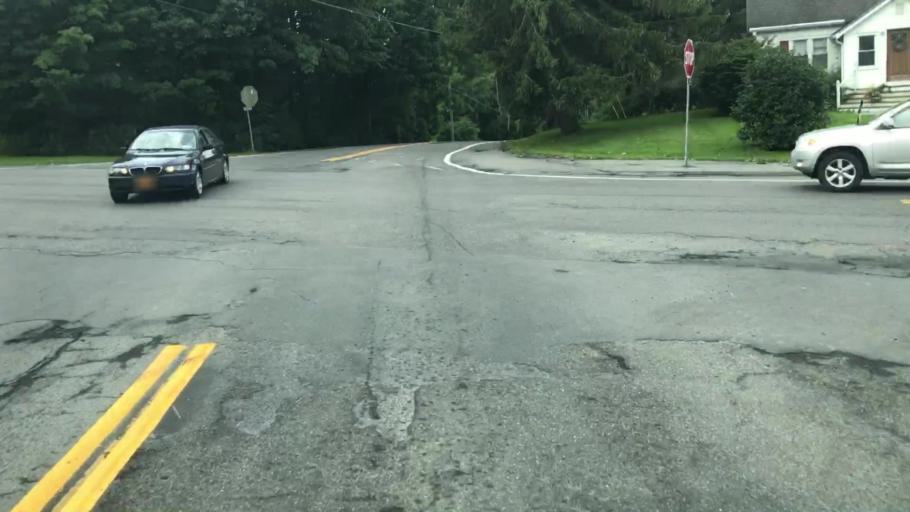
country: US
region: New York
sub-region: Onondaga County
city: Skaneateles
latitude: 42.9634
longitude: -76.4359
